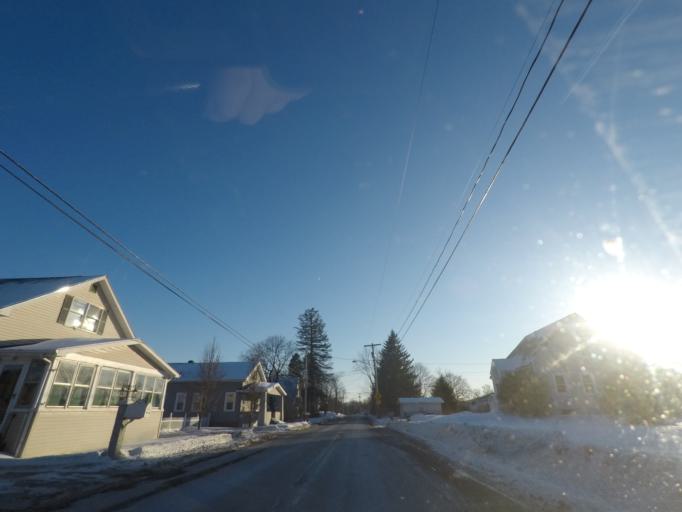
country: US
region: New York
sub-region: Saratoga County
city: Mechanicville
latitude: 42.9019
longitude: -73.6775
